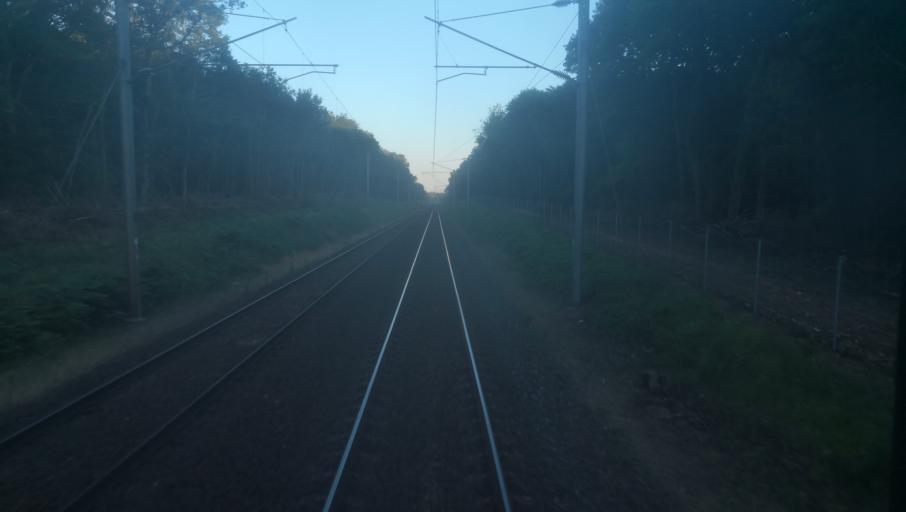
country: FR
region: Bourgogne
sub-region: Departement de la Nievre
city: La Charite-sur-Loire
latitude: 47.2148
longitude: 3.0183
